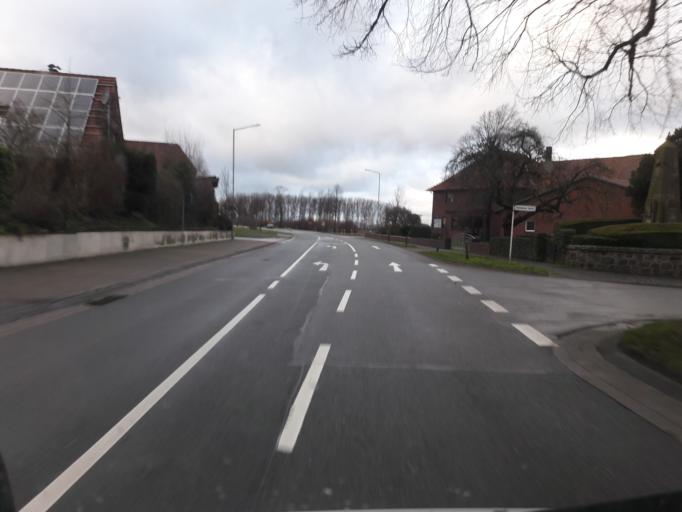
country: DE
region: North Rhine-Westphalia
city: Bad Oeynhausen
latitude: 52.2770
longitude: 8.8298
